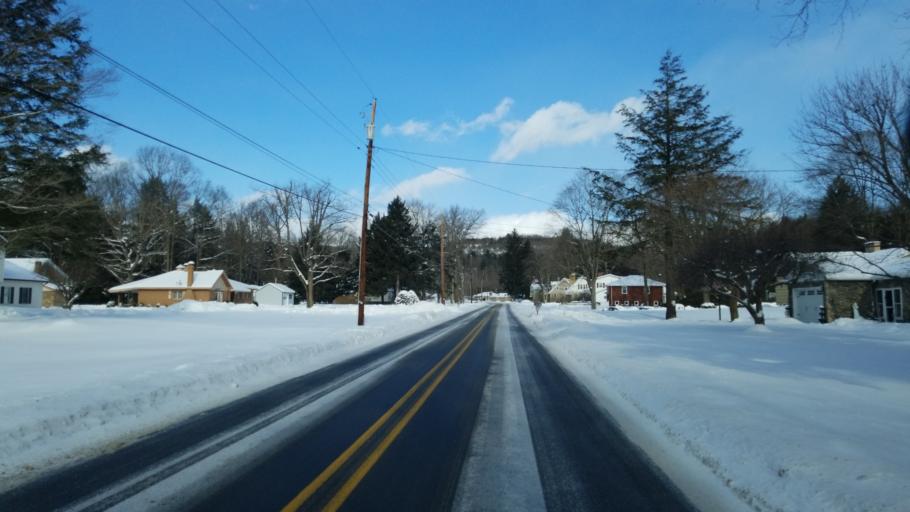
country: US
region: Pennsylvania
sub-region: Clearfield County
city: Hyde
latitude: 41.0095
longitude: -78.4696
